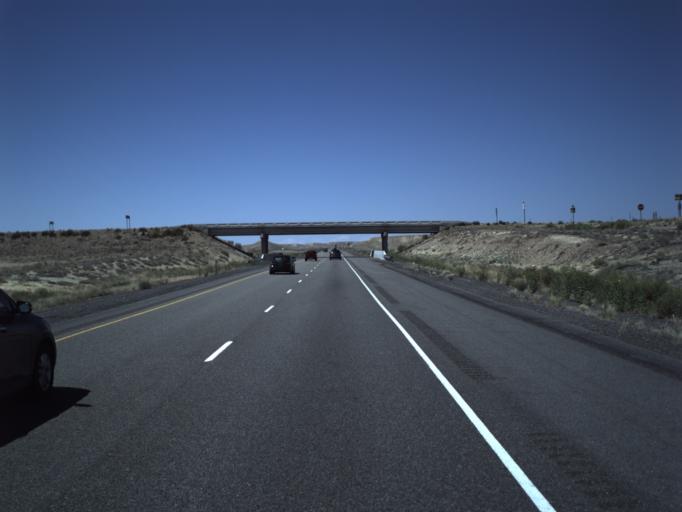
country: US
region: Utah
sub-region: Grand County
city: Moab
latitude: 38.9428
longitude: -109.6125
